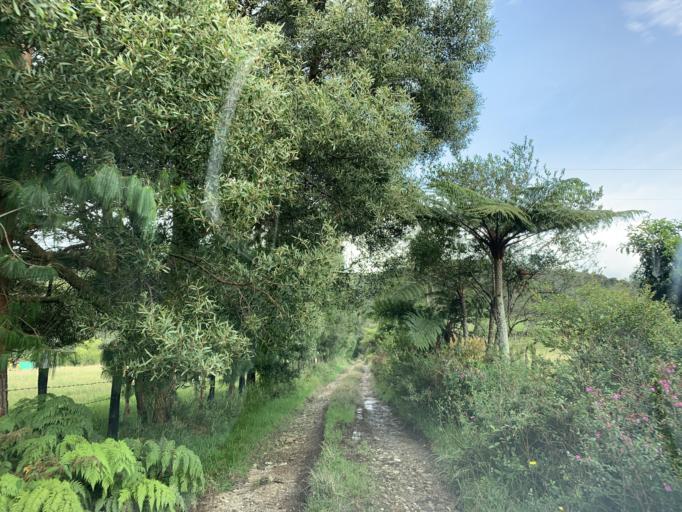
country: CO
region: Boyaca
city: Arcabuco
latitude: 5.7929
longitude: -73.4558
